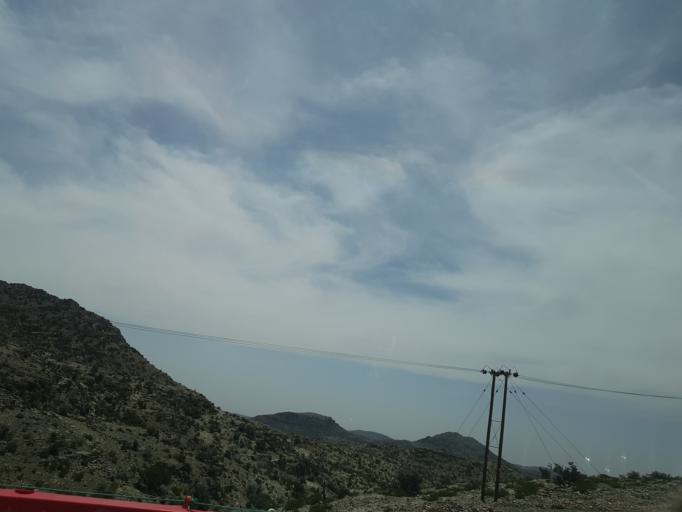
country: OM
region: Muhafazat ad Dakhiliyah
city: Nizwa
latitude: 23.1154
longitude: 57.6467
